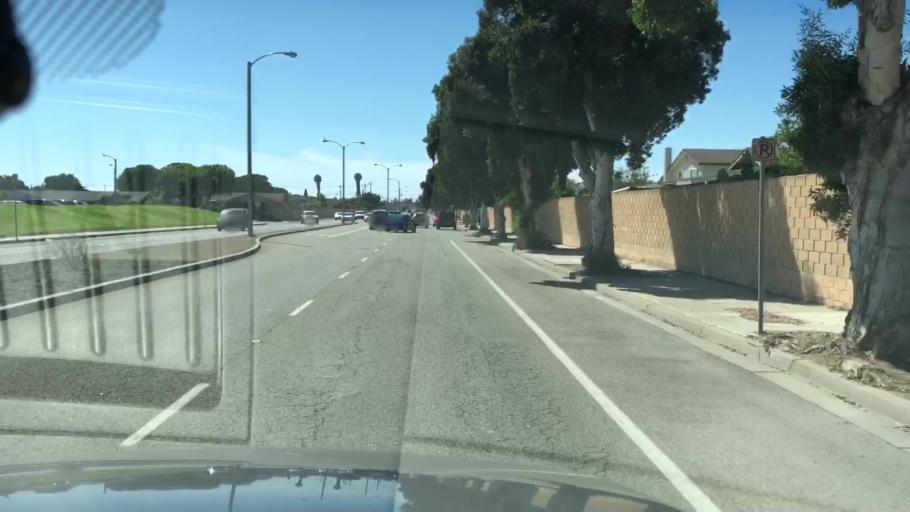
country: US
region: California
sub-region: Ventura County
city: Port Hueneme
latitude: 34.1623
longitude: -119.1616
